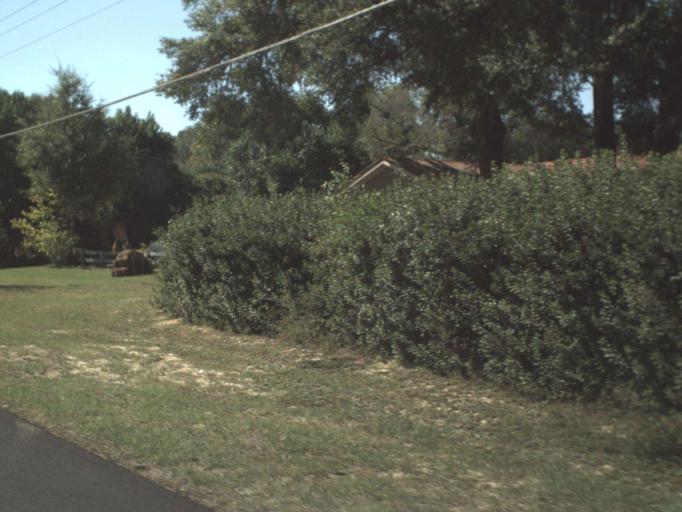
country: US
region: Florida
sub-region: Walton County
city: DeFuniak Springs
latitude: 30.7503
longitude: -86.1141
